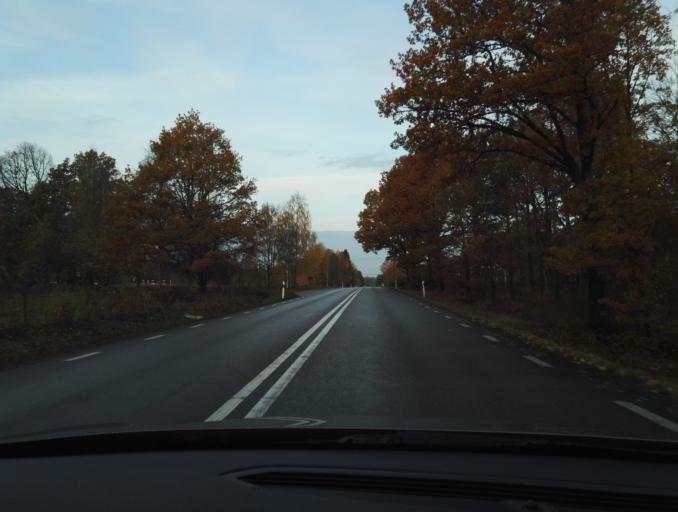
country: SE
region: Kronoberg
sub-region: Alvesta Kommun
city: Moheda
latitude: 56.9895
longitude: 14.6893
